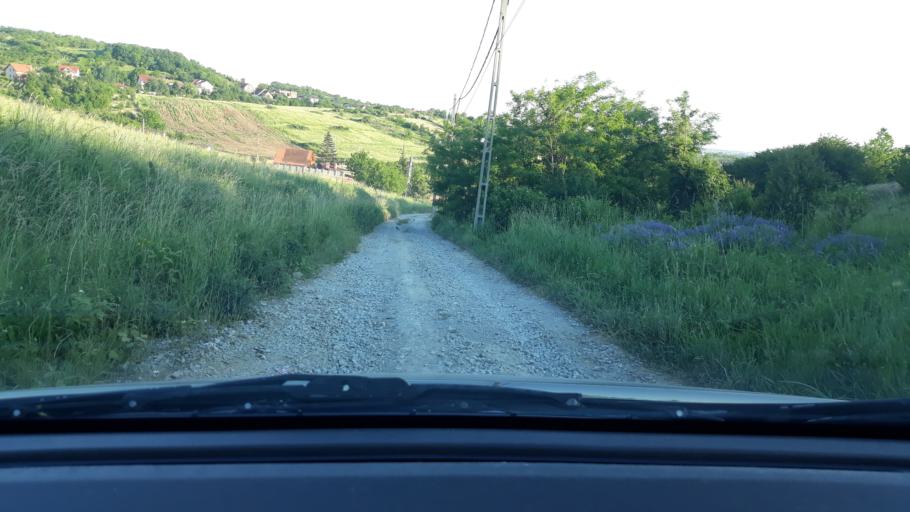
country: RO
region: Bihor
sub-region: Comuna Paleu
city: Paleu
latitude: 47.1003
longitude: 21.9348
